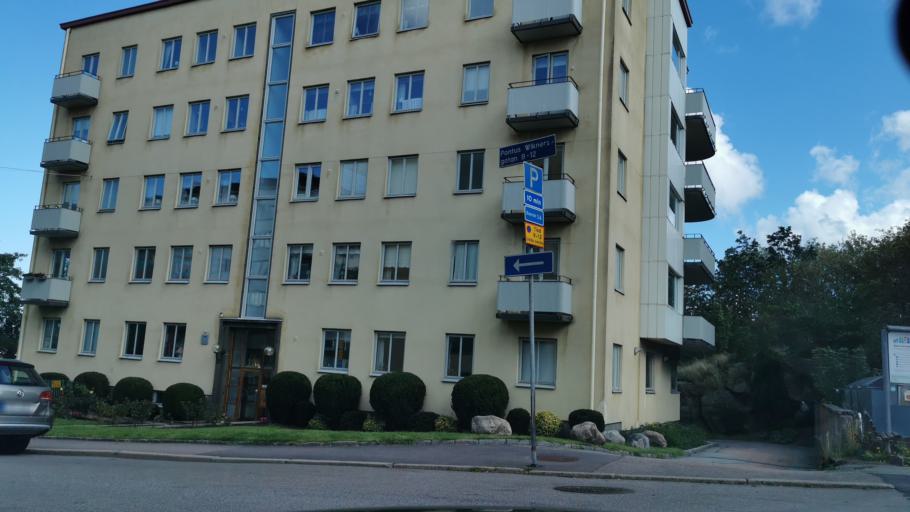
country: SE
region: Vaestra Goetaland
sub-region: Goteborg
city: Goeteborg
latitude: 57.6927
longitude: 11.9811
